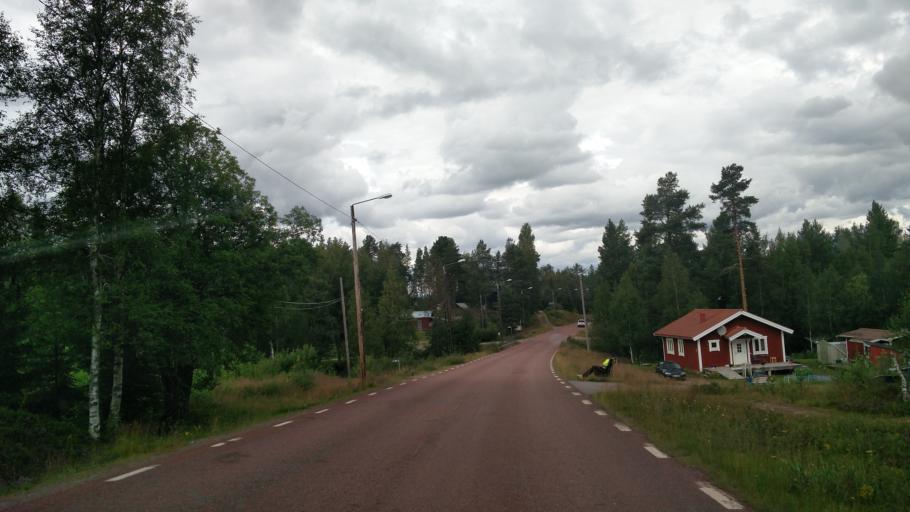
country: NO
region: Hedmark
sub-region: Trysil
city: Innbygda
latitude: 61.1357
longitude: 12.8083
